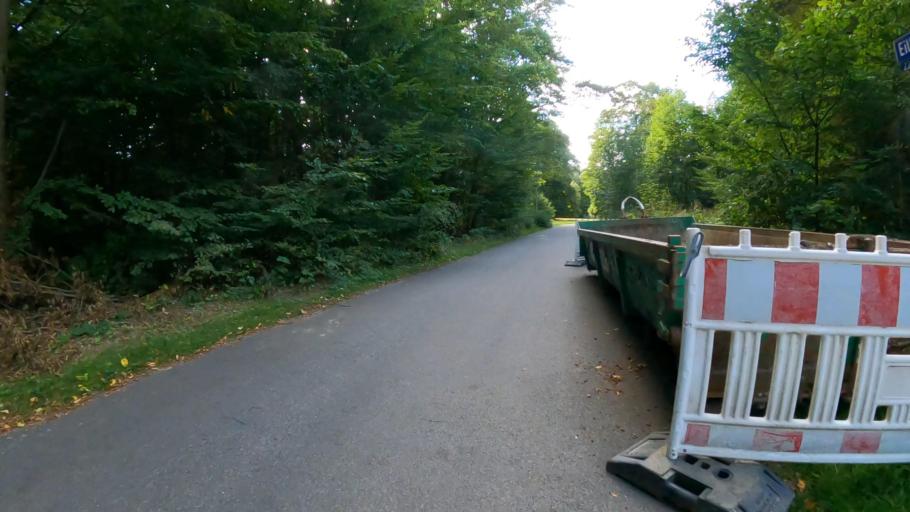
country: DE
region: Schleswig-Holstein
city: Grosshansdorf
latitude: 53.6591
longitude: 10.2915
